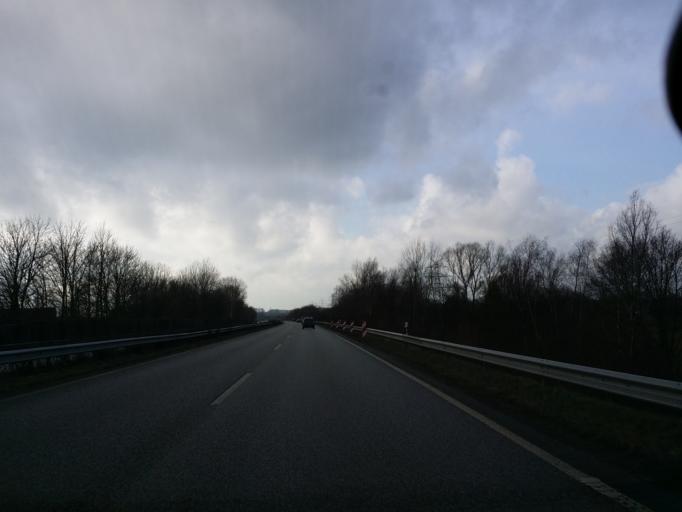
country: DE
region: Schleswig-Holstein
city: Quarnbek
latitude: 54.3193
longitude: 9.9799
